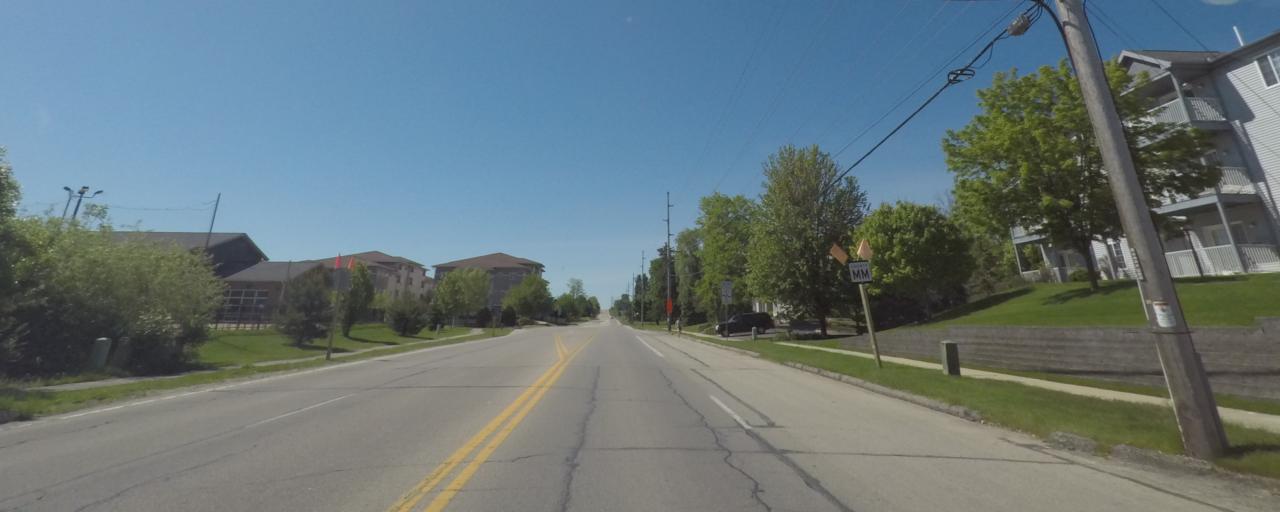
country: US
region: Wisconsin
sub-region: Dane County
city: Oregon
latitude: 42.9172
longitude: -89.3739
